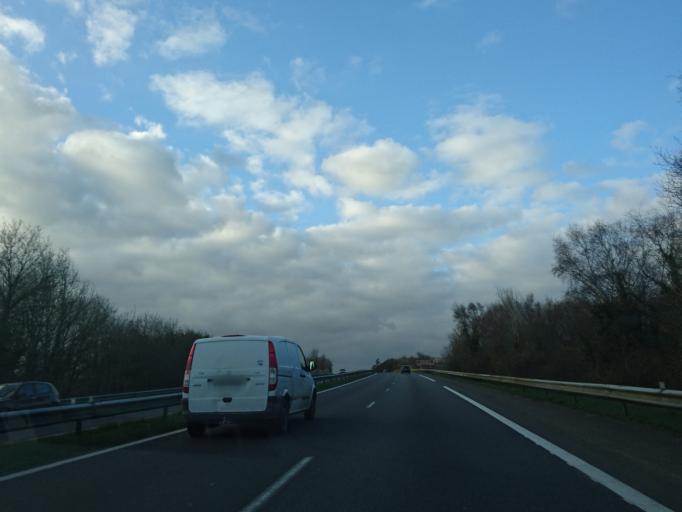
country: FR
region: Brittany
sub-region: Departement du Finistere
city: Hopital-Camfrout
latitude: 48.3480
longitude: -4.2334
